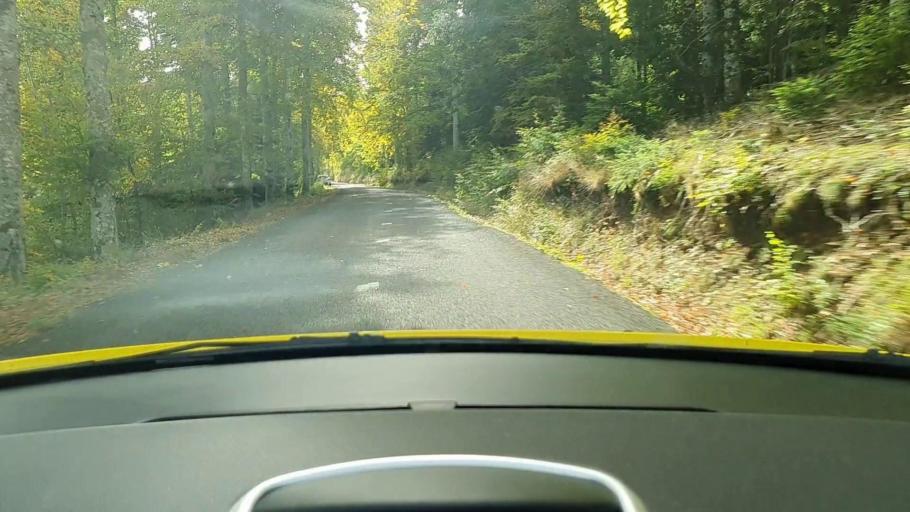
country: FR
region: Languedoc-Roussillon
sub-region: Departement du Gard
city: Valleraugue
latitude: 44.0732
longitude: 3.5673
